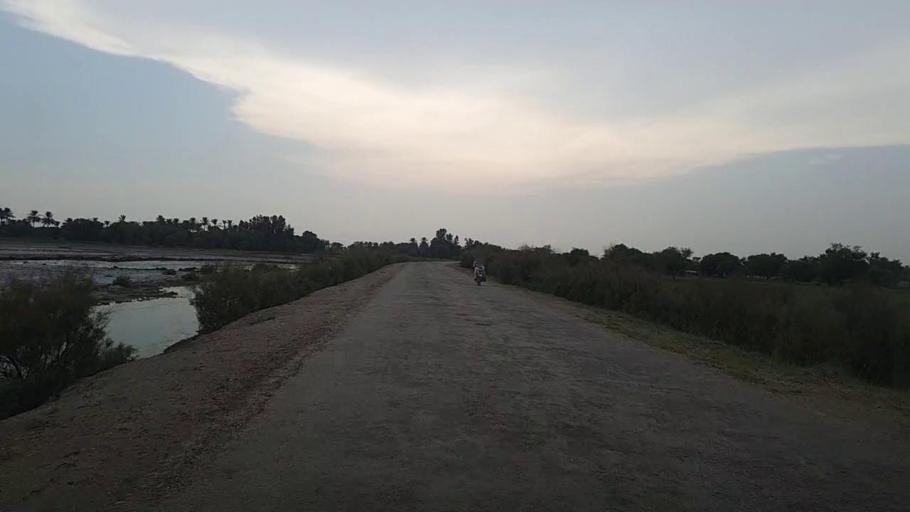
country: PK
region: Sindh
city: Khanpur
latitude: 27.8378
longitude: 69.4734
